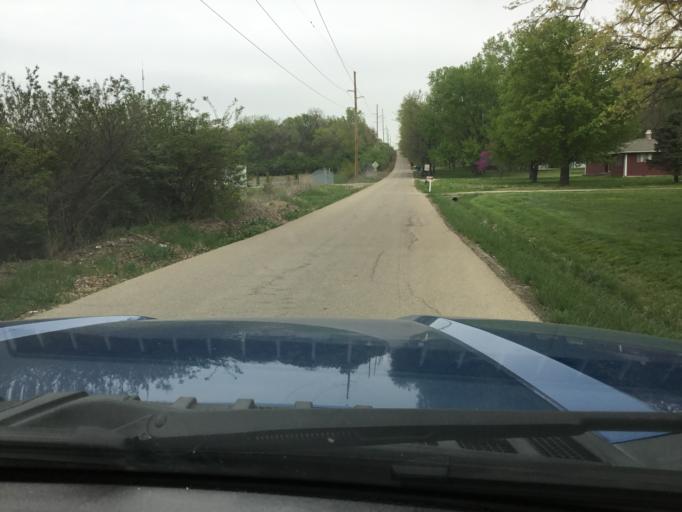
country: US
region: Kansas
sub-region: Shawnee County
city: Topeka
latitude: 39.1022
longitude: -95.6874
